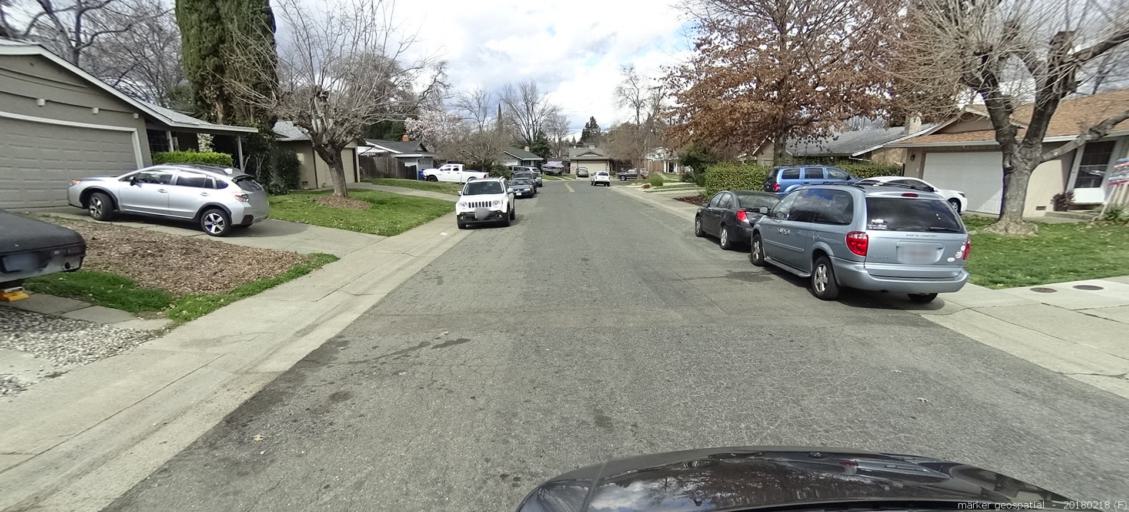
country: US
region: California
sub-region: Sacramento County
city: Orangevale
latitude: 38.6691
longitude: -121.2183
